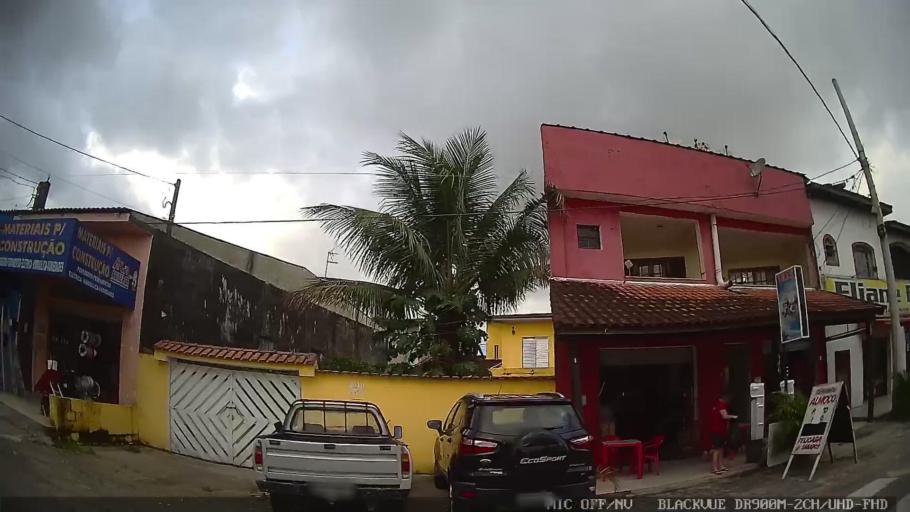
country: BR
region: Sao Paulo
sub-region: Itanhaem
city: Itanhaem
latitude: -24.1632
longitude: -46.7832
